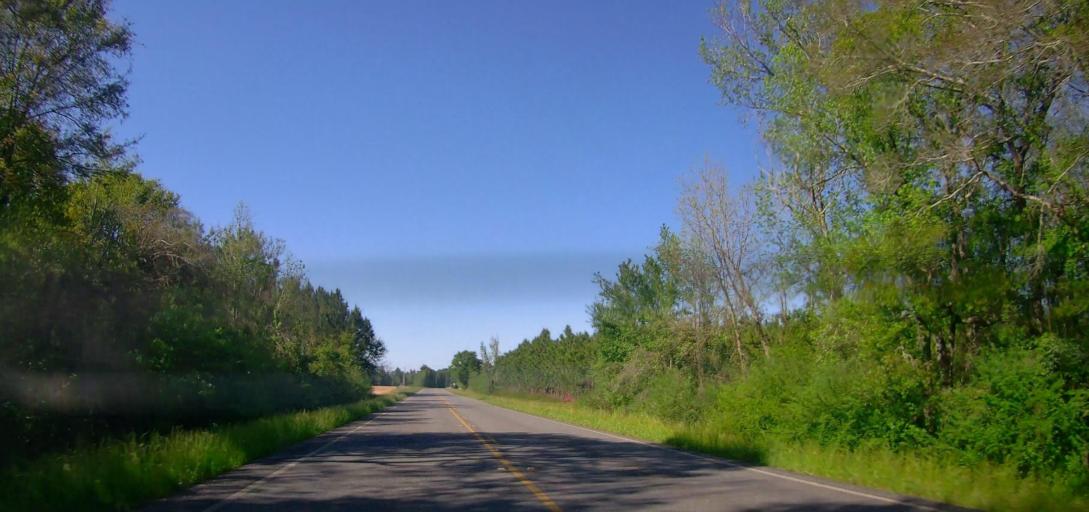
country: US
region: Georgia
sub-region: Wilcox County
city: Rochelle
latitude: 32.0945
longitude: -83.5032
